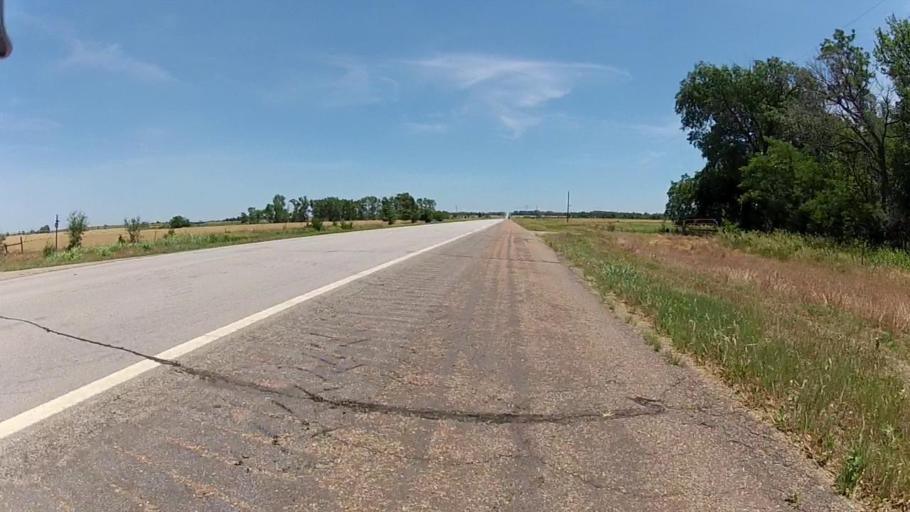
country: US
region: Kansas
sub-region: Barber County
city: Medicine Lodge
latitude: 37.2533
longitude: -98.3236
